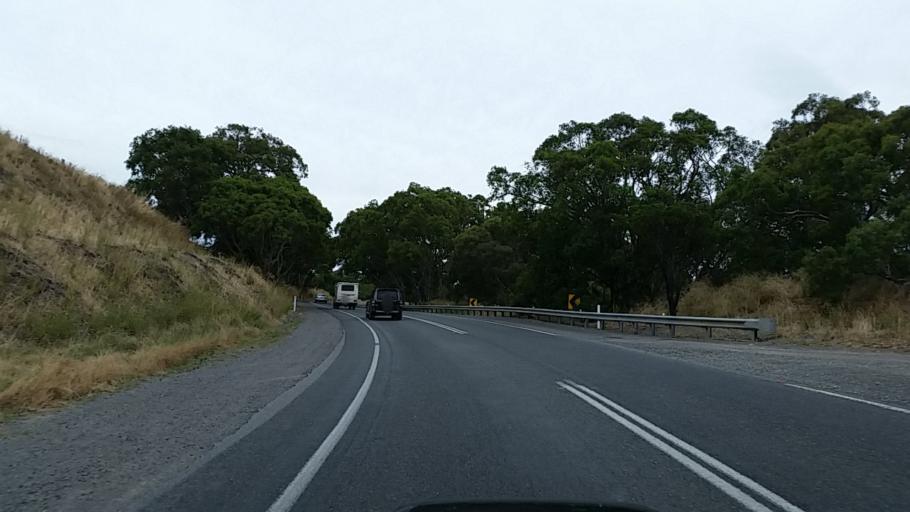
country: AU
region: South Australia
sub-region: Onkaparinga
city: Aldinga
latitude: -35.3661
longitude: 138.4565
